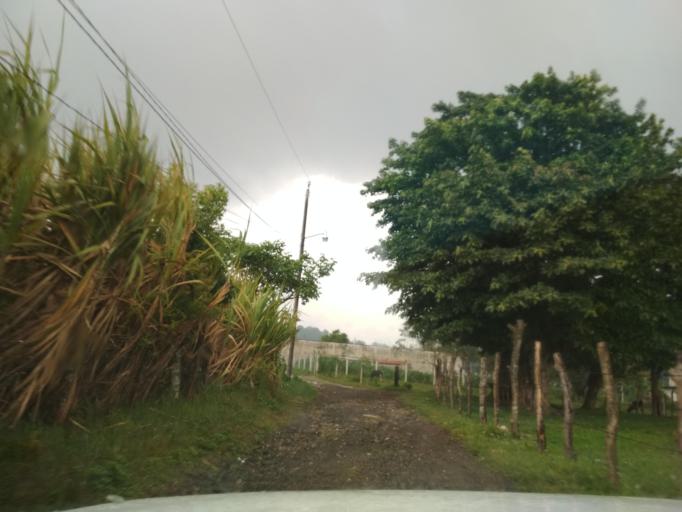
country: MX
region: Veracruz
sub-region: Mariano Escobedo
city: Chicola
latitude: 18.9047
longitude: -97.1167
